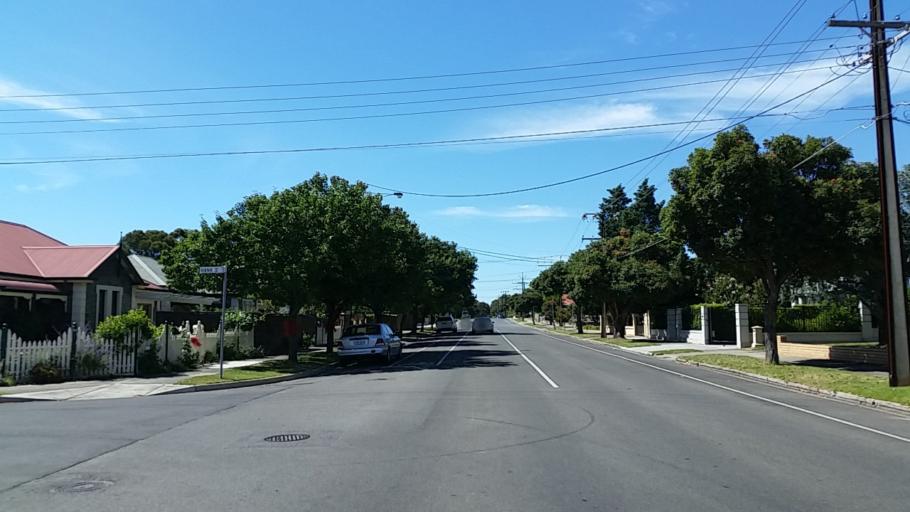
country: AU
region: South Australia
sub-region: Charles Sturt
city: Findon
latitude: -34.9220
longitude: 138.5287
